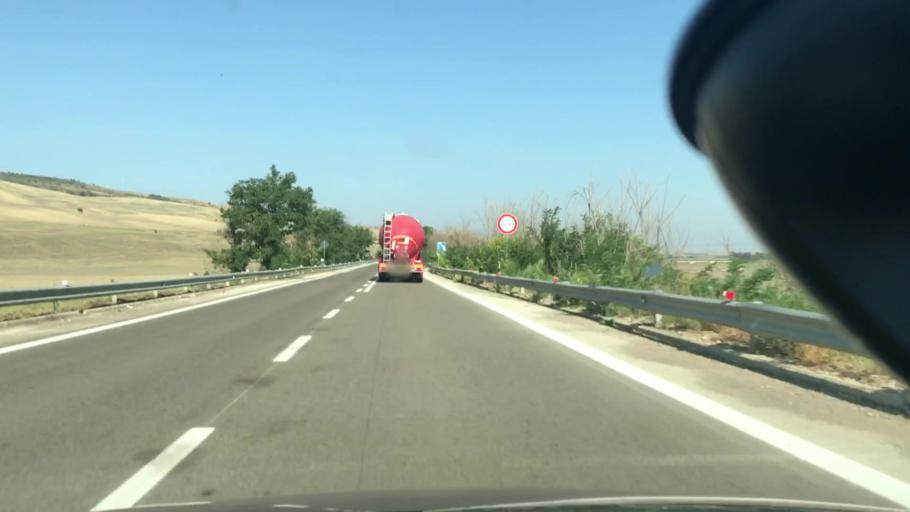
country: IT
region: Basilicate
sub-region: Provincia di Matera
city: Irsina
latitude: 40.7926
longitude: 16.2805
